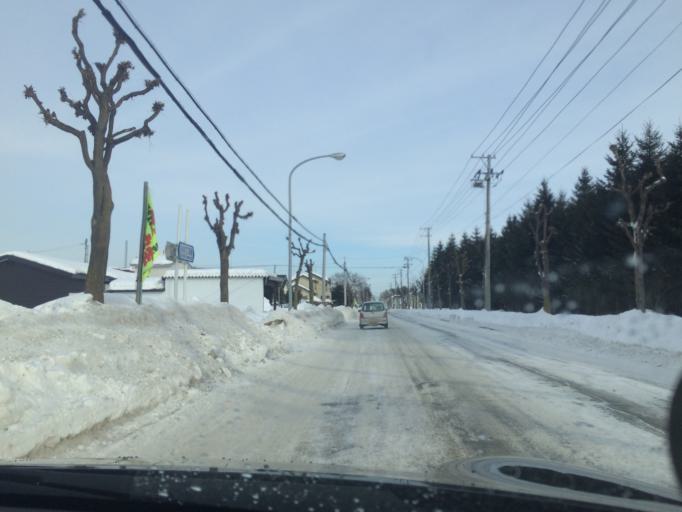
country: JP
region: Hokkaido
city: Obihiro
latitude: 42.9099
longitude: 143.0364
